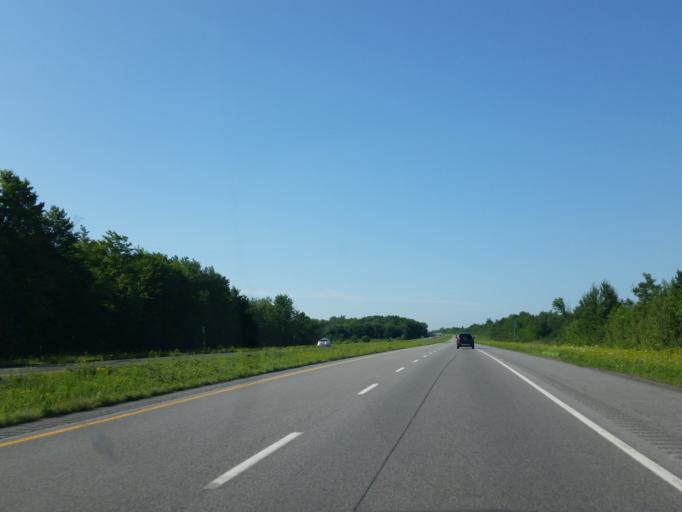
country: CA
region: Quebec
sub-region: Monteregie
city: Napierville
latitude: 45.2573
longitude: -73.4700
